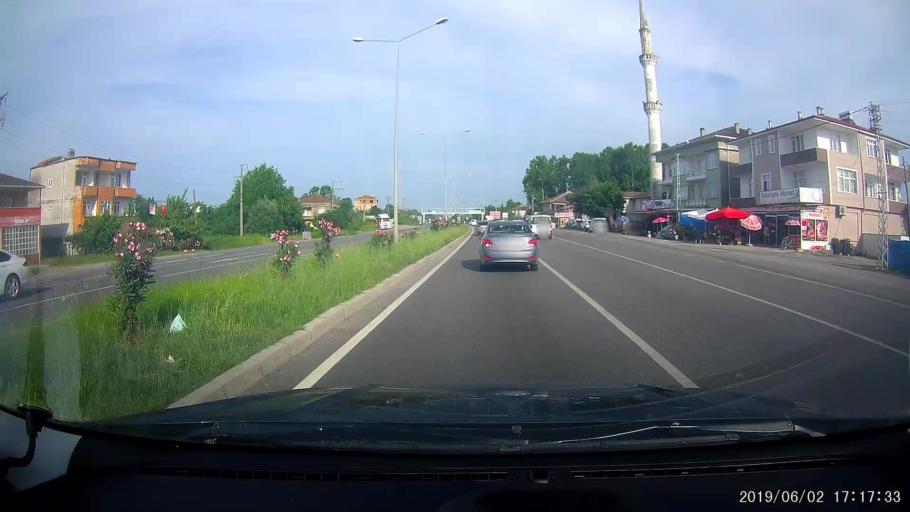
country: TR
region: Samsun
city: Dikbiyik
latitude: 41.2276
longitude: 36.5842
